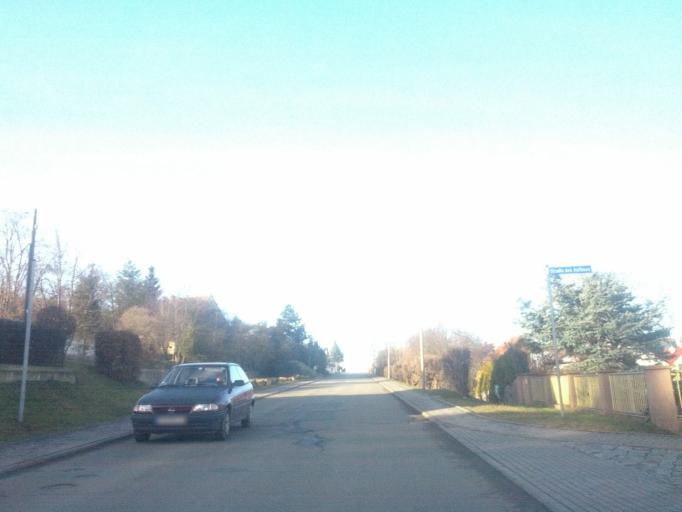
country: DE
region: Thuringia
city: Seebergen
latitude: 50.9245
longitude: 10.7971
